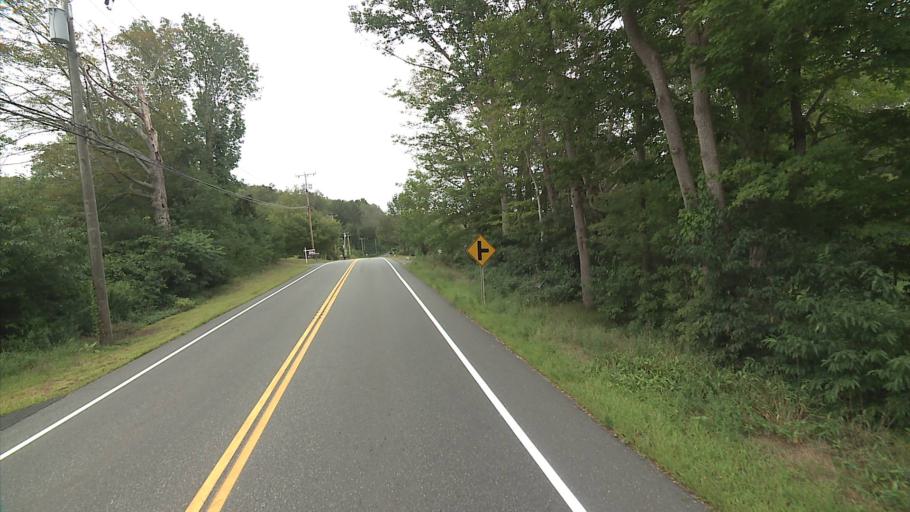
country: US
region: Connecticut
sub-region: New London County
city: Colchester
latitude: 41.5080
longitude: -72.2895
